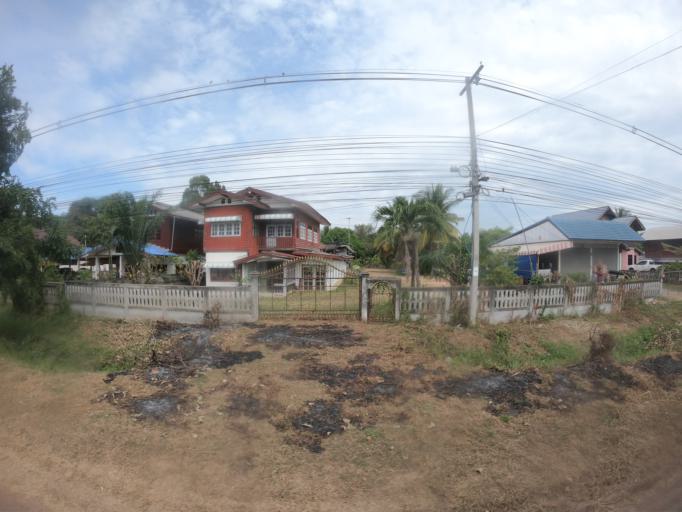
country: TH
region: Maha Sarakham
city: Chiang Yuen
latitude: 16.3447
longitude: 103.1269
